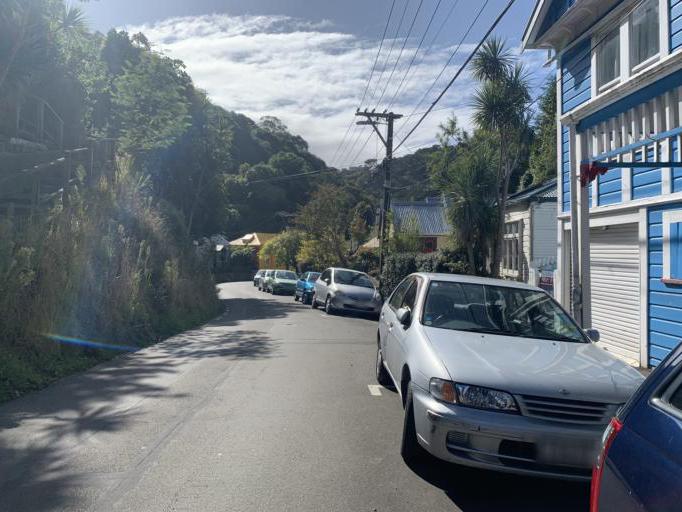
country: NZ
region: Wellington
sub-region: Wellington City
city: Kelburn
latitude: -41.2949
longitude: 174.7586
